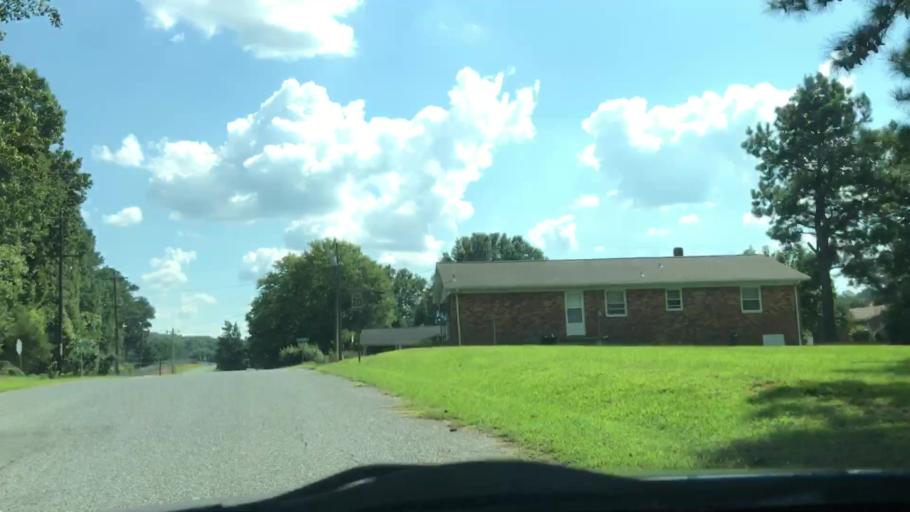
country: US
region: North Carolina
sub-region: Randolph County
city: Asheboro
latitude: 35.7502
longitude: -79.8142
